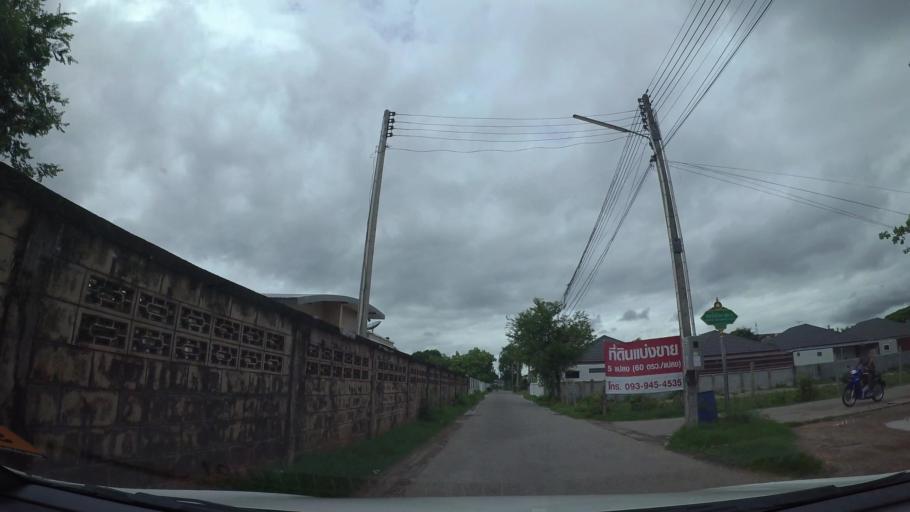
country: TH
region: Rayong
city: Rayong
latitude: 12.6653
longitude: 101.2777
